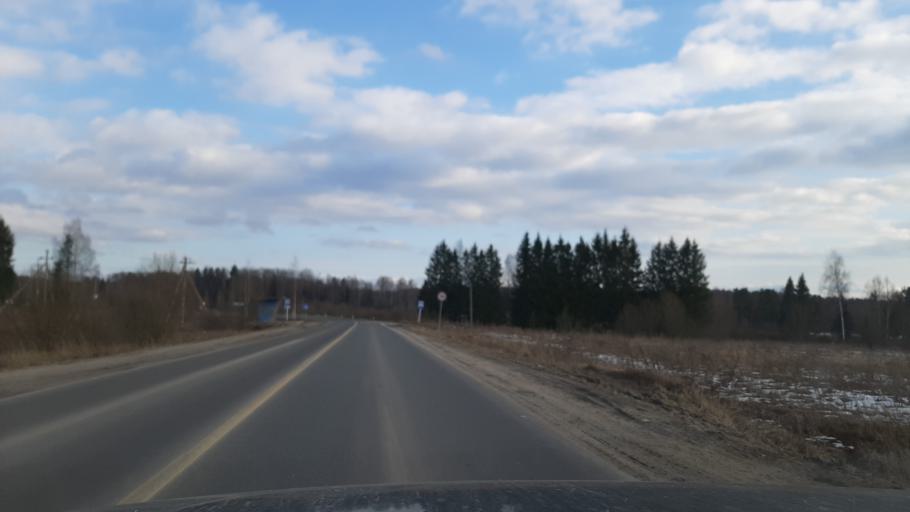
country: RU
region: Ivanovo
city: Novo-Talitsy
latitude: 56.9404
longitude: 40.7127
